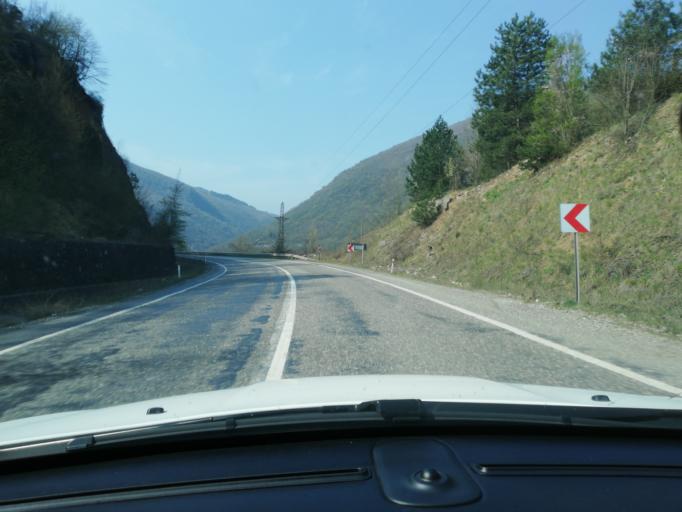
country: TR
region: Karabuk
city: Yenice
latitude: 41.2085
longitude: 32.3608
